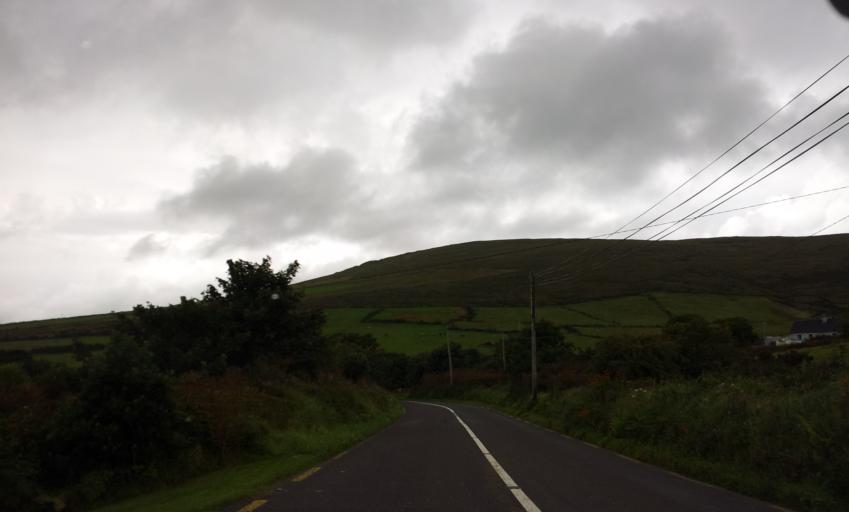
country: IE
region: Munster
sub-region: Ciarrai
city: Killorglin
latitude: 52.1829
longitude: -9.9646
